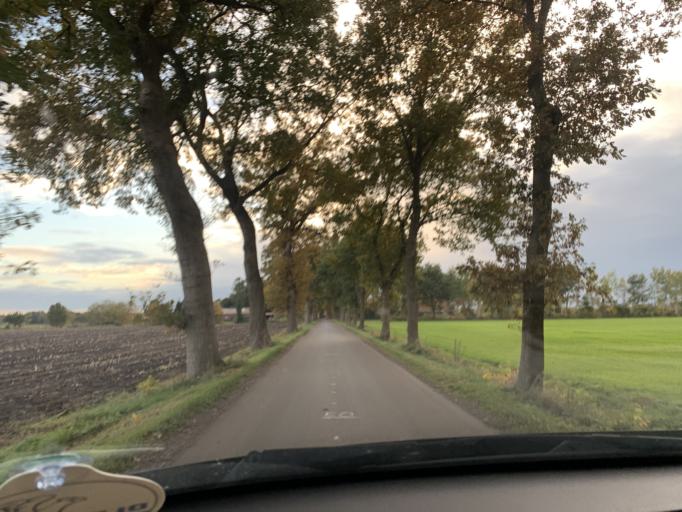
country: DE
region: Lower Saxony
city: Wiefelstede
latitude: 53.2668
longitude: 8.0726
